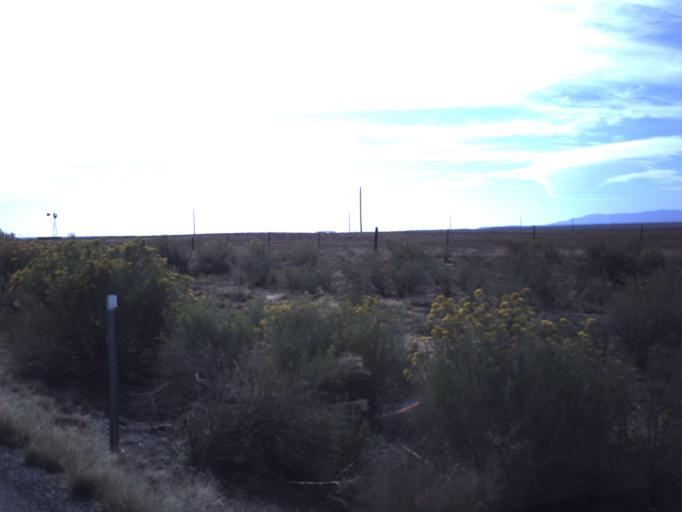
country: US
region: Utah
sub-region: San Juan County
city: Blanding
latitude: 37.4336
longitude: -109.3721
